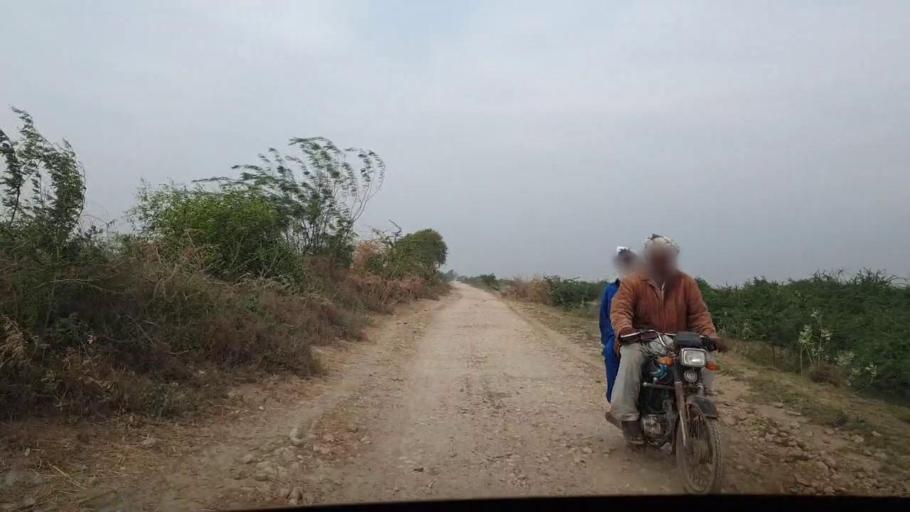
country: PK
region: Sindh
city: Chuhar Jamali
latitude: 24.4089
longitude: 67.9505
